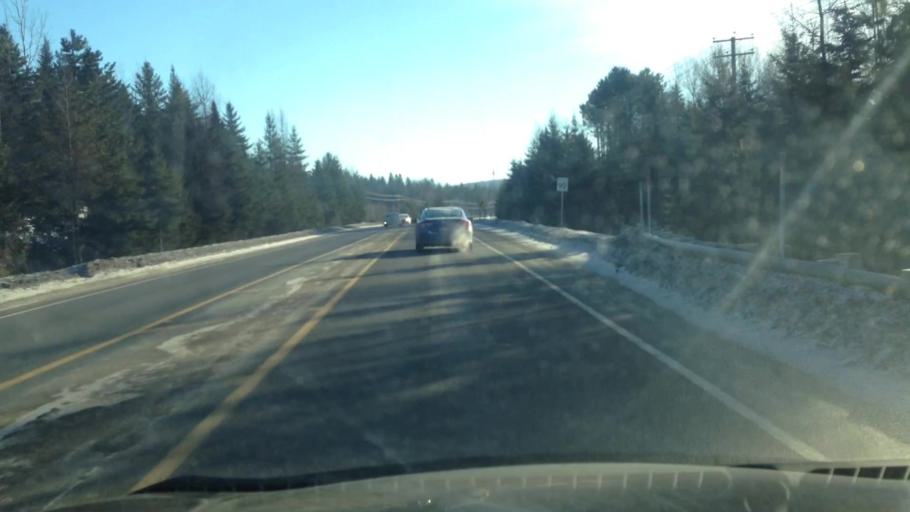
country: CA
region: Quebec
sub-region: Laurentides
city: Saint-Sauveur
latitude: 45.8948
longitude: -74.2006
